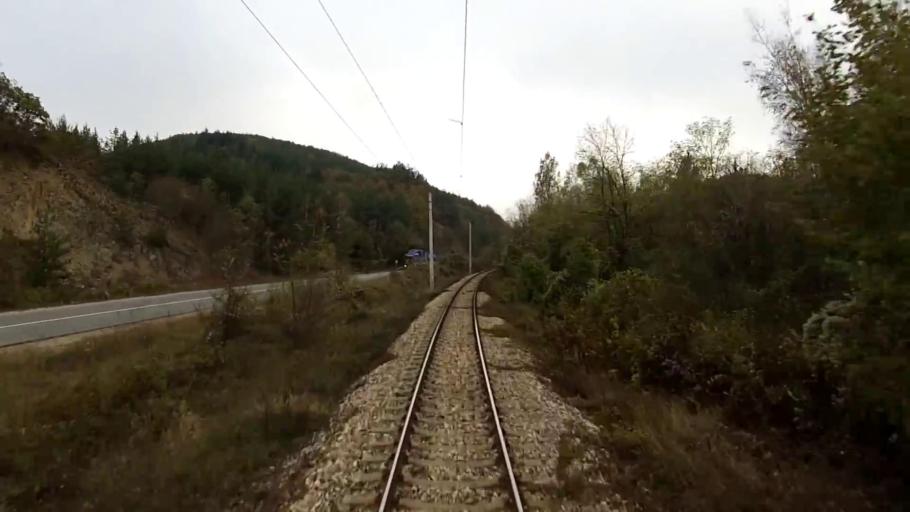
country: BG
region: Sofiya
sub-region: Obshtina Dragoman
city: Dragoman
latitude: 42.9526
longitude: 22.9043
